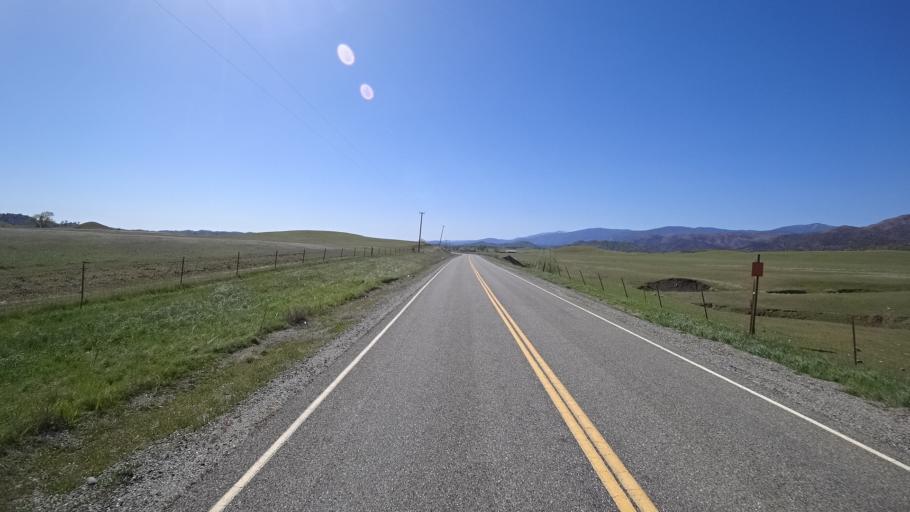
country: US
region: California
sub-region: Tehama County
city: Rancho Tehama Reserve
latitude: 39.7100
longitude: -122.5500
